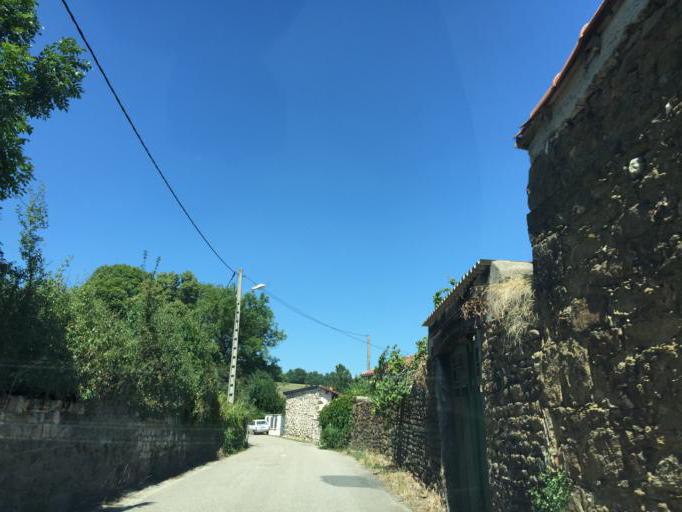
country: FR
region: Rhone-Alpes
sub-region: Departement de la Loire
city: Saint-Jean-Bonnefonds
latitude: 45.4620
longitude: 4.4581
